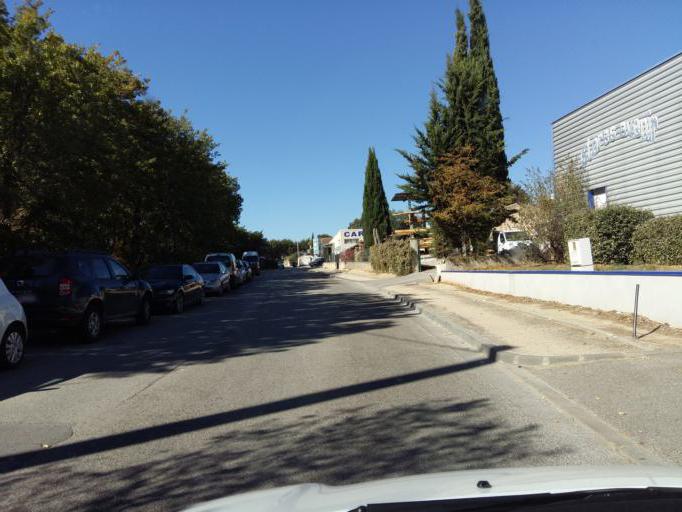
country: FR
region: Provence-Alpes-Cote d'Azur
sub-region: Departement du Vaucluse
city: Pertuis
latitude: 43.7200
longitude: 5.5385
